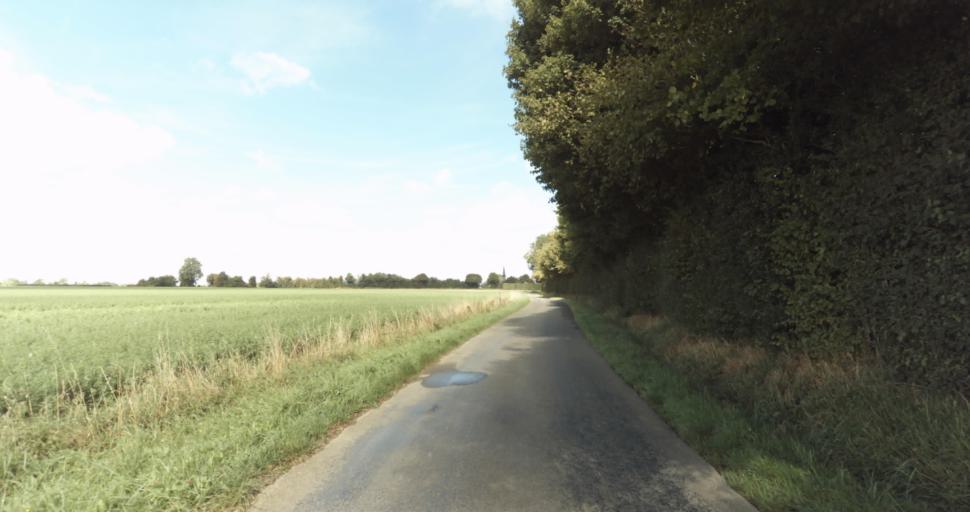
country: FR
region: Lower Normandy
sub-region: Departement du Calvados
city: Orbec
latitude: 48.9371
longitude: 0.3813
